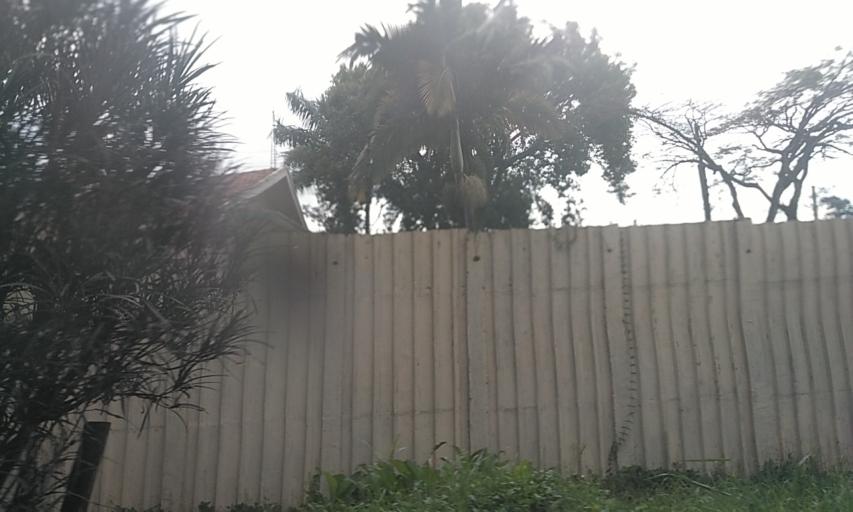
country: UG
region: Central Region
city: Kampala Central Division
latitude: 0.3343
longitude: 32.5863
